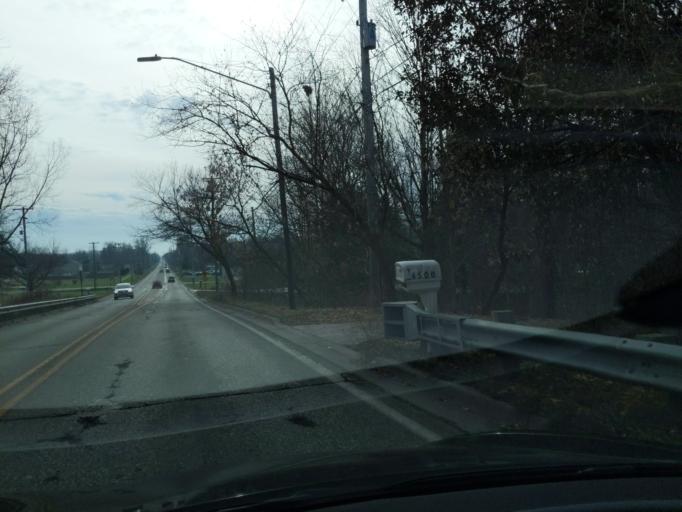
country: US
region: Michigan
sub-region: Ingham County
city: Holt
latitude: 42.6633
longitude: -84.5236
